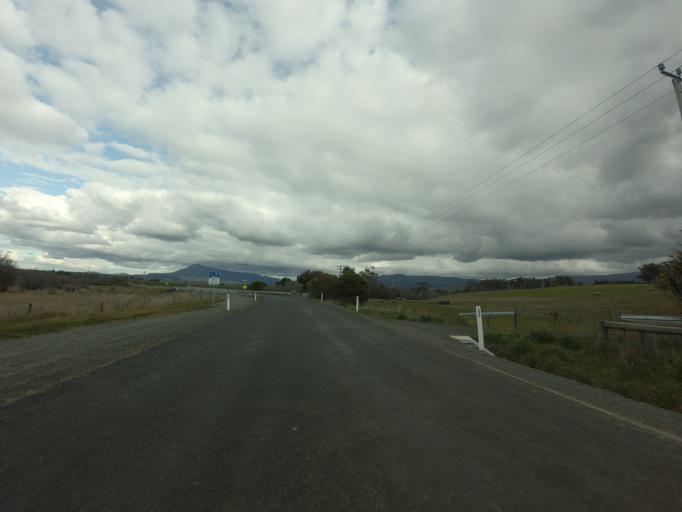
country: AU
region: Tasmania
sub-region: Northern Midlands
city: Longford
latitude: -41.7821
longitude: 147.0969
